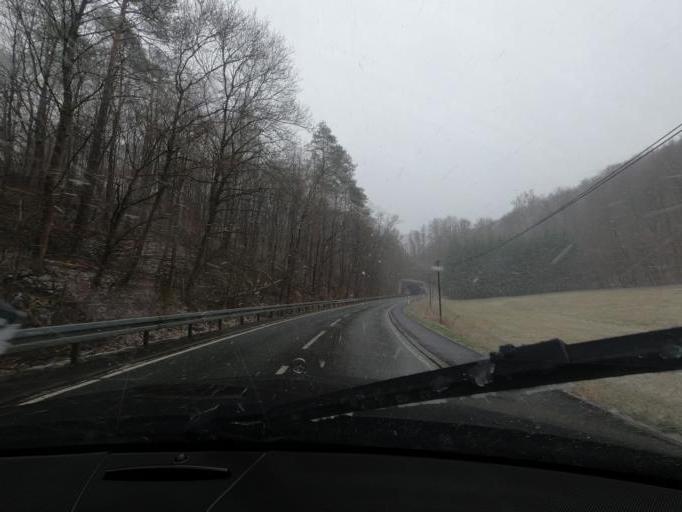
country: DE
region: Thuringia
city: Effelder
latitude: 51.2539
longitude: 10.2414
